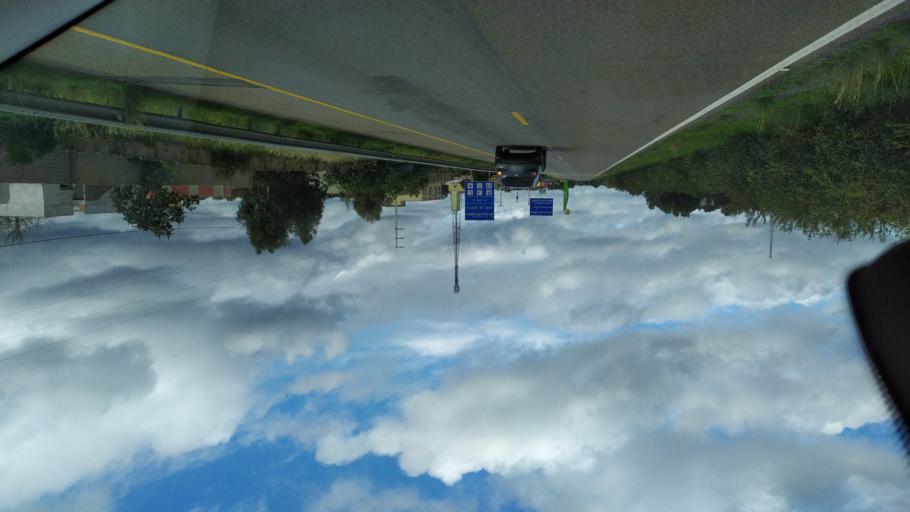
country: MA
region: Gharb-Chrarda-Beni Hssen
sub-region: Kenitra Province
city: Lalla Mimouna
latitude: 34.8712
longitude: -6.2165
